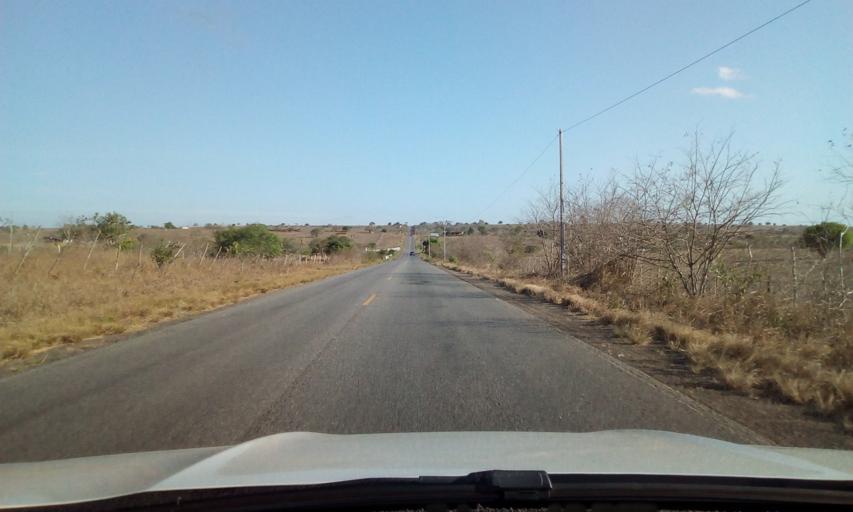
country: BR
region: Paraiba
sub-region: Mulungu
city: Mulungu
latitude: -6.9687
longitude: -35.4051
